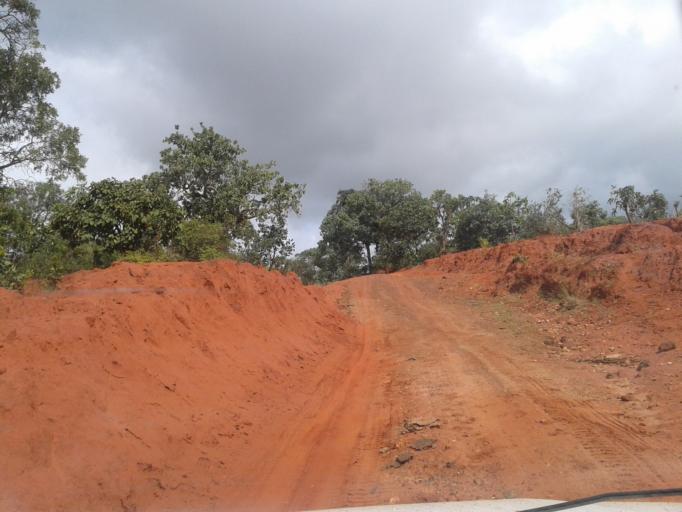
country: BR
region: Minas Gerais
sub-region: Campina Verde
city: Campina Verde
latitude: -19.4145
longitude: -49.6627
